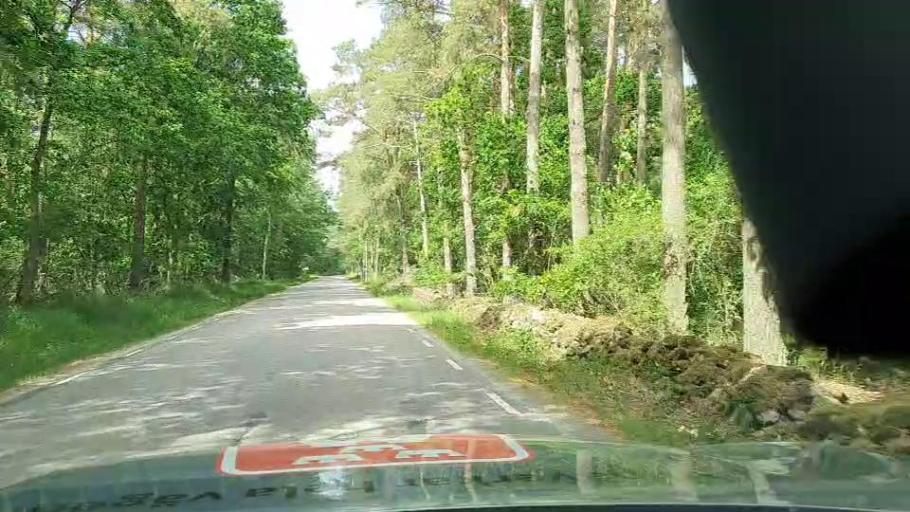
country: SE
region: Blekinge
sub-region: Karlshamns Kommun
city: Morrum
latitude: 56.1001
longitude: 14.6868
